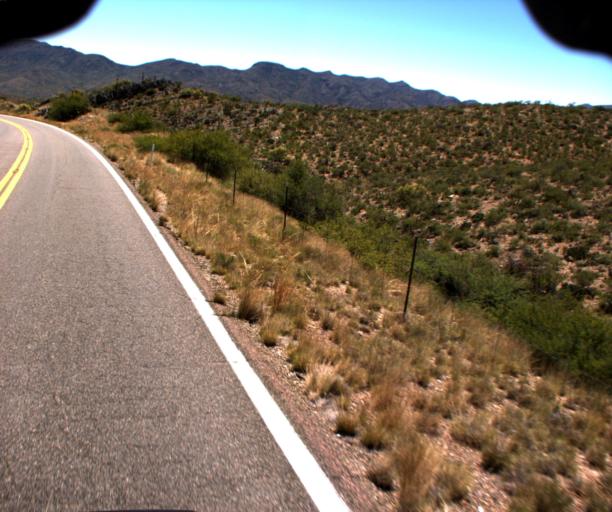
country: US
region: Arizona
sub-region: Pinal County
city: Kearny
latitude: 33.1833
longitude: -110.8113
